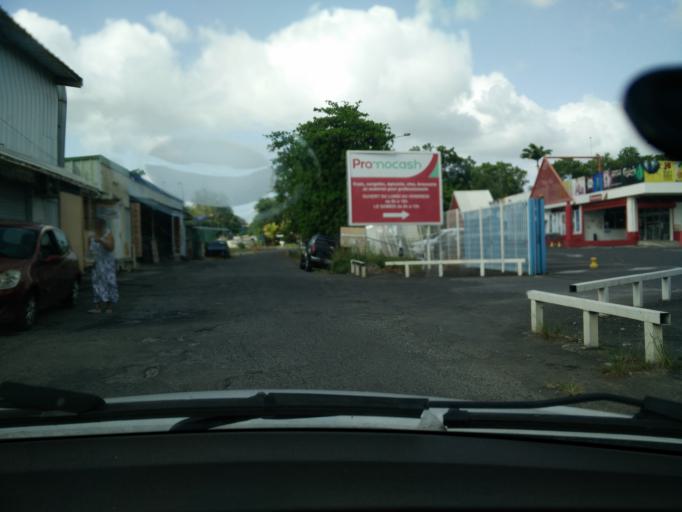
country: GP
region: Guadeloupe
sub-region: Guadeloupe
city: Pointe-a-Pitre
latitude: 16.2584
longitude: -61.5246
